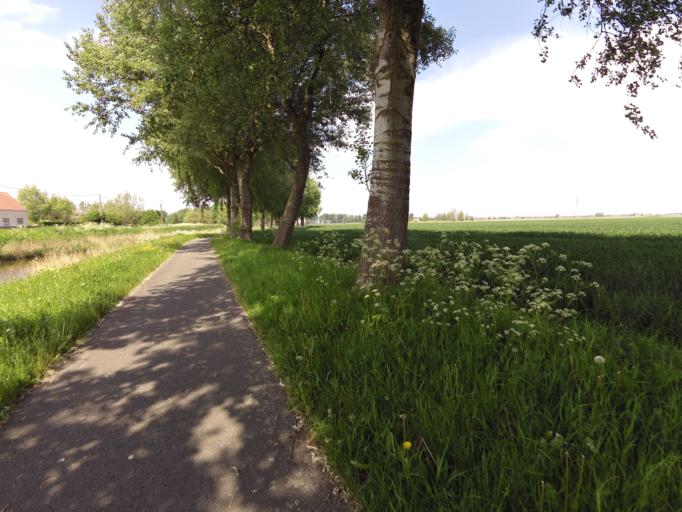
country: BE
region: Flanders
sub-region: Provincie West-Vlaanderen
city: Bredene
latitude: 51.2190
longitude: 2.9966
